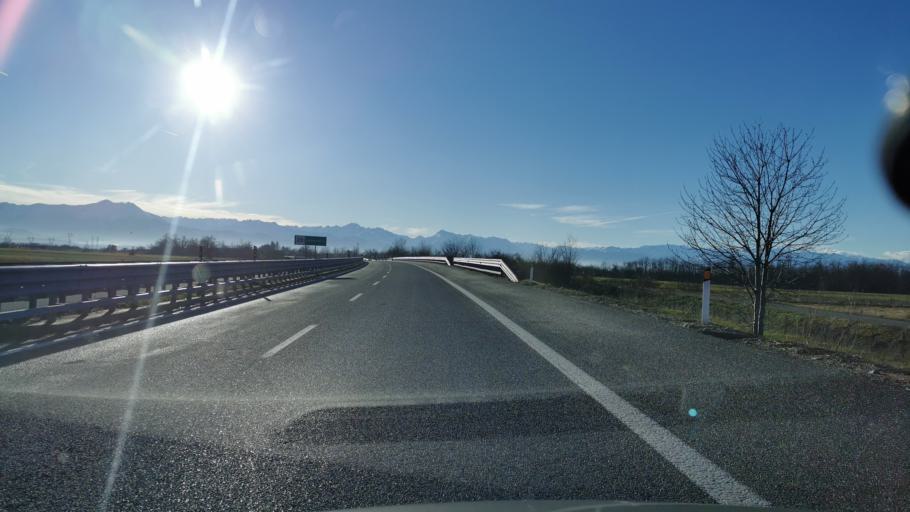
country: IT
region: Piedmont
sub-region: Provincia di Cuneo
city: Magliano Alpi
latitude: 44.4821
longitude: 7.7986
